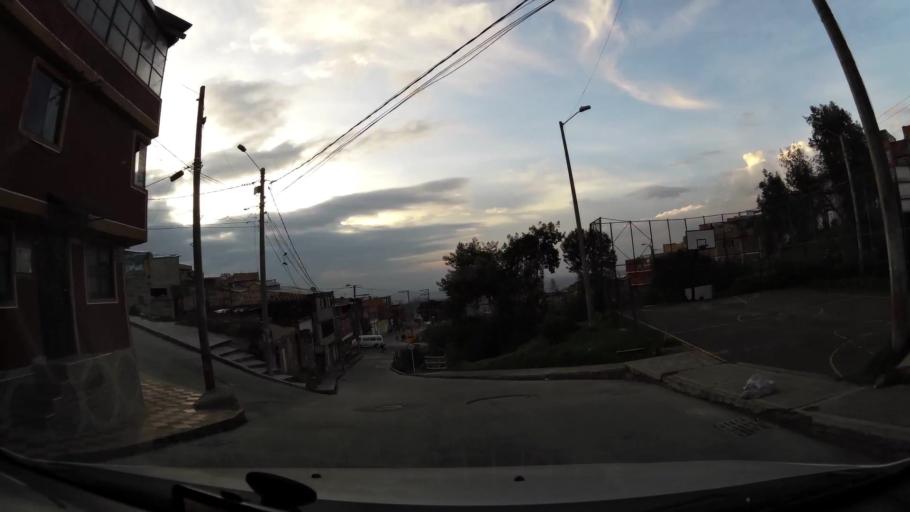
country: CO
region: Bogota D.C.
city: Bogota
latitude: 4.5404
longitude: -74.0870
